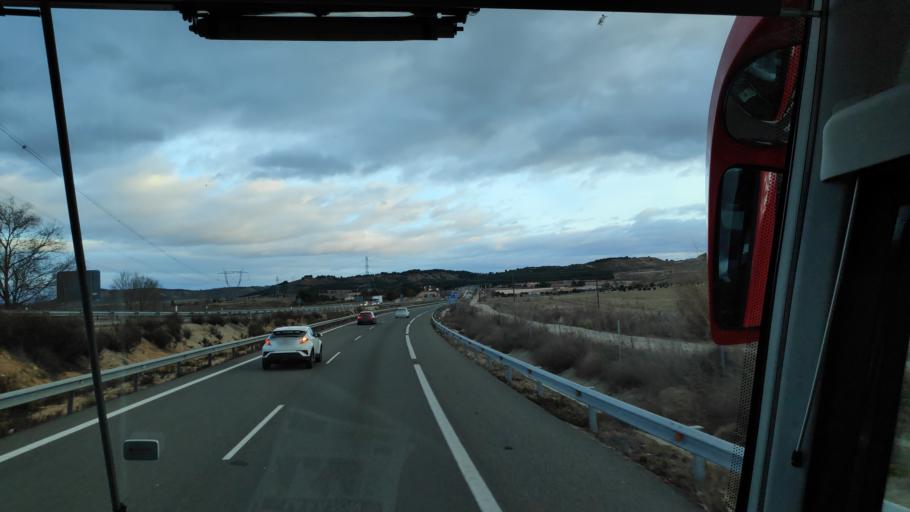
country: ES
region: Castille-La Mancha
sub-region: Provincia de Cuenca
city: Belinchon
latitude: 40.0417
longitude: -3.0541
